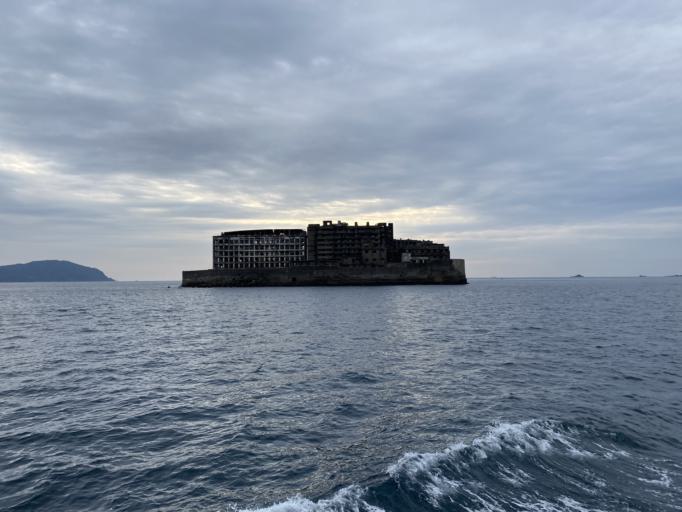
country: JP
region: Nagasaki
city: Nagasaki-shi
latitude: 32.6314
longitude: 129.7407
